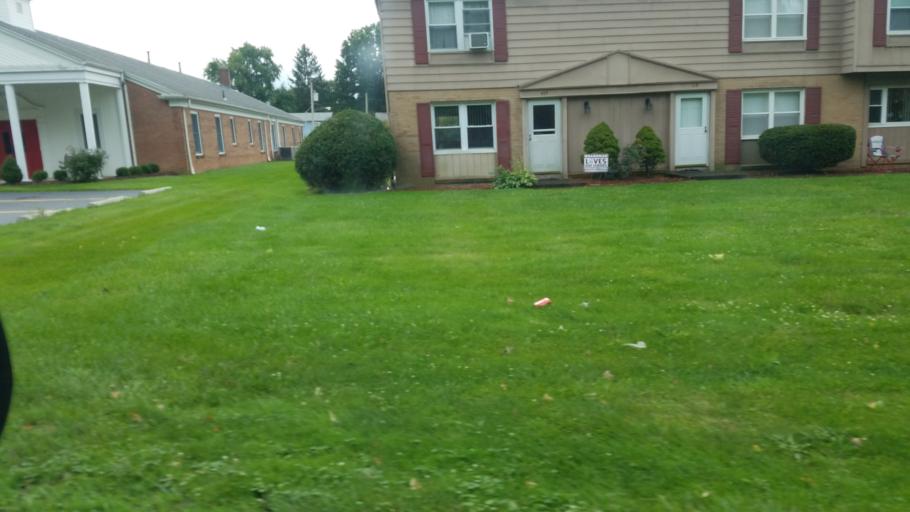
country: US
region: Ohio
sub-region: Mahoning County
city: Boardman
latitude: 41.0389
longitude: -80.6423
